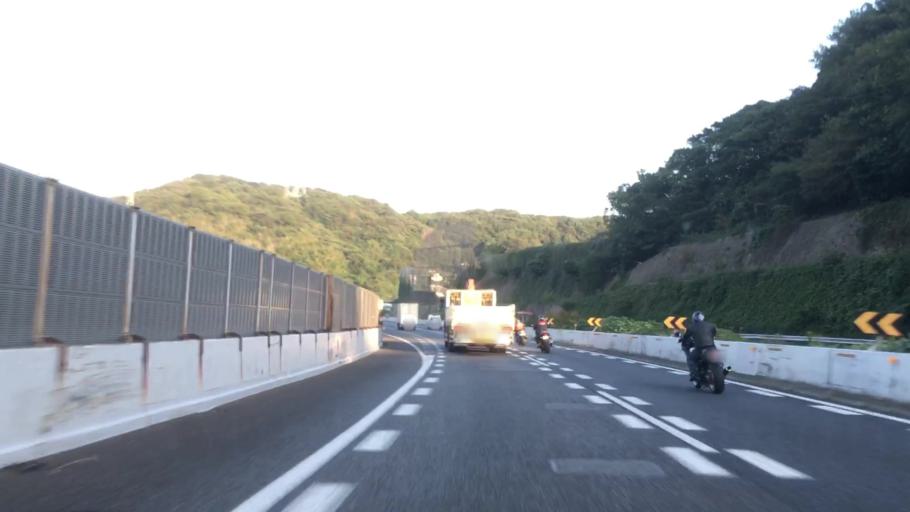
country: JP
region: Yamaguchi
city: Shimonoseki
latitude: 33.9544
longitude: 130.9738
